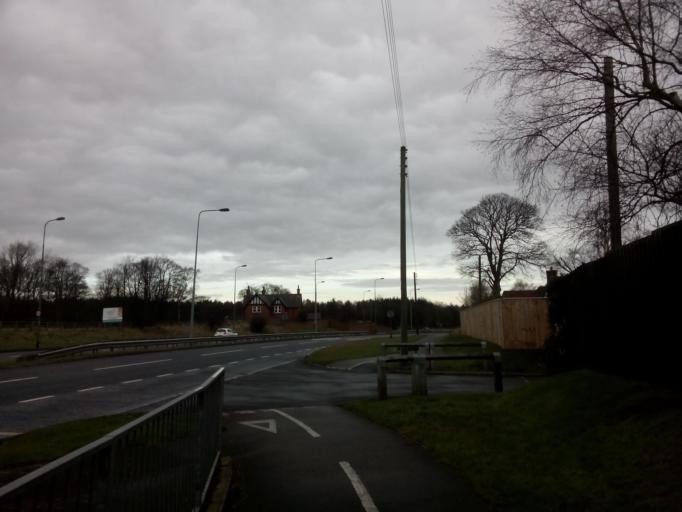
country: GB
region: England
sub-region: County Durham
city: Chester-le-Street
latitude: 54.8388
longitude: -1.5851
